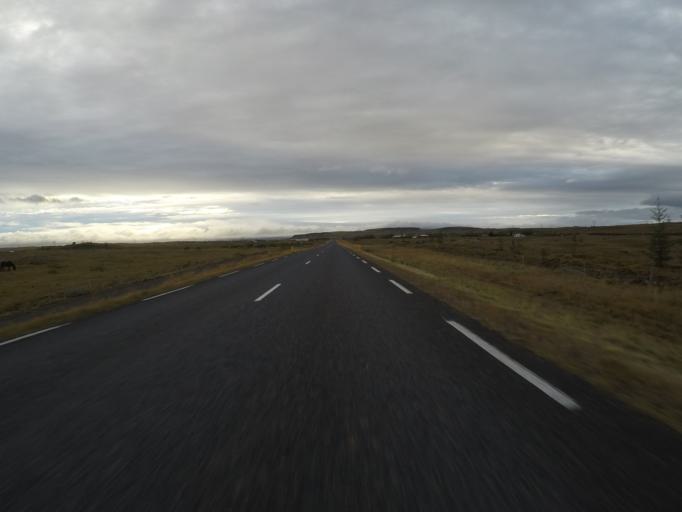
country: IS
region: South
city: Vestmannaeyjar
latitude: 64.0411
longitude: -20.2303
